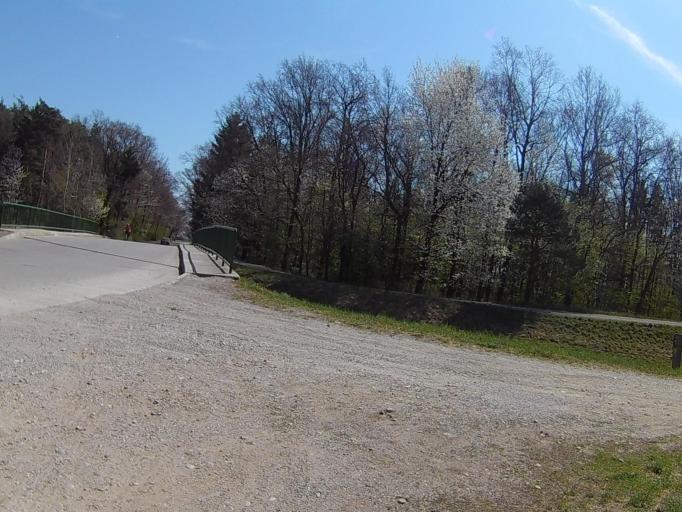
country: SI
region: Hoce-Slivnica
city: Rogoza
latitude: 46.4941
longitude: 15.6855
